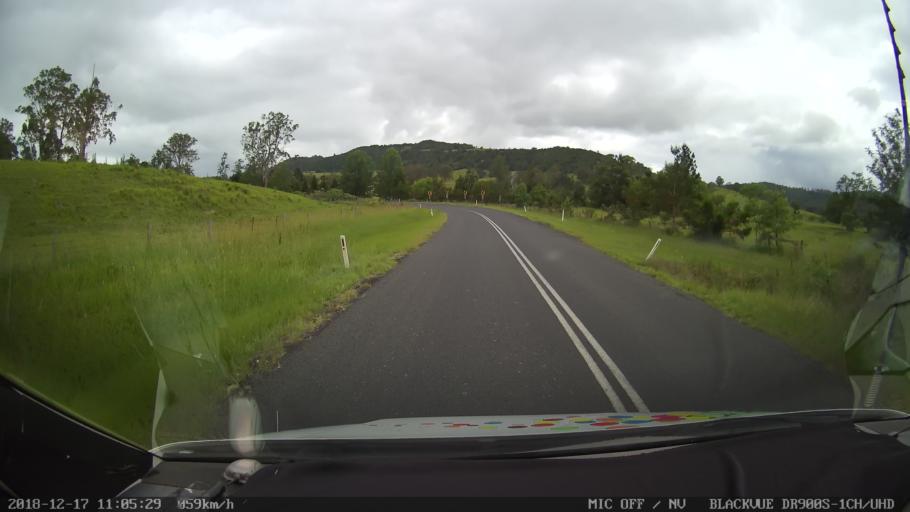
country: AU
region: New South Wales
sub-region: Kyogle
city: Kyogle
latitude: -28.7898
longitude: 152.6472
